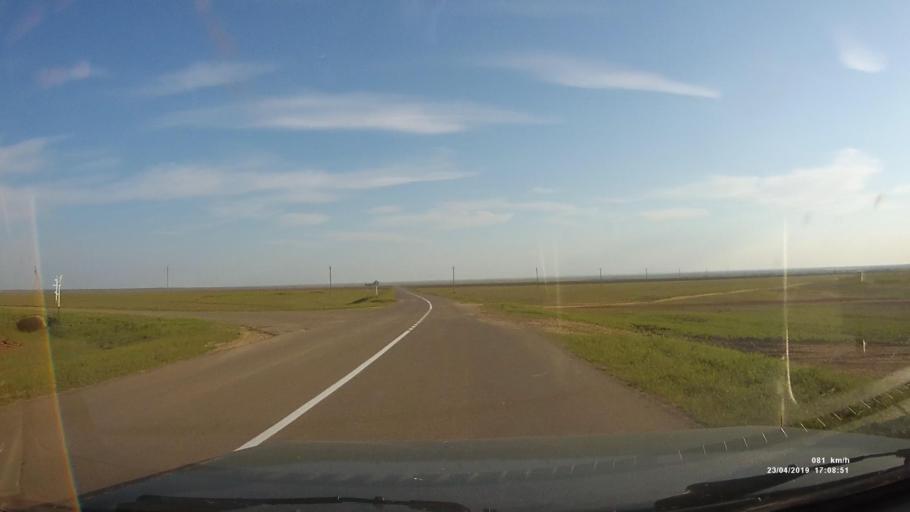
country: RU
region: Kalmykiya
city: Priyutnoye
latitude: 46.2662
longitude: 43.4845
